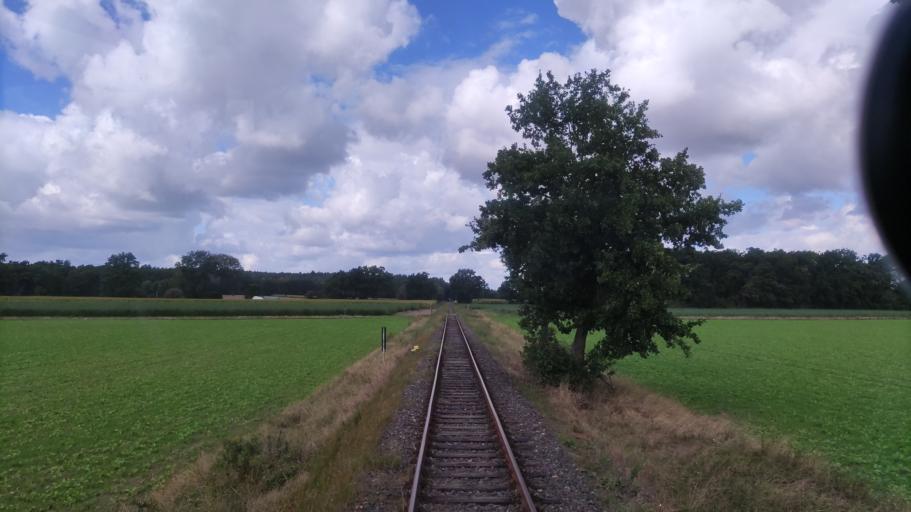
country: DE
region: Lower Saxony
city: Neetze
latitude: 53.2706
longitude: 10.6180
